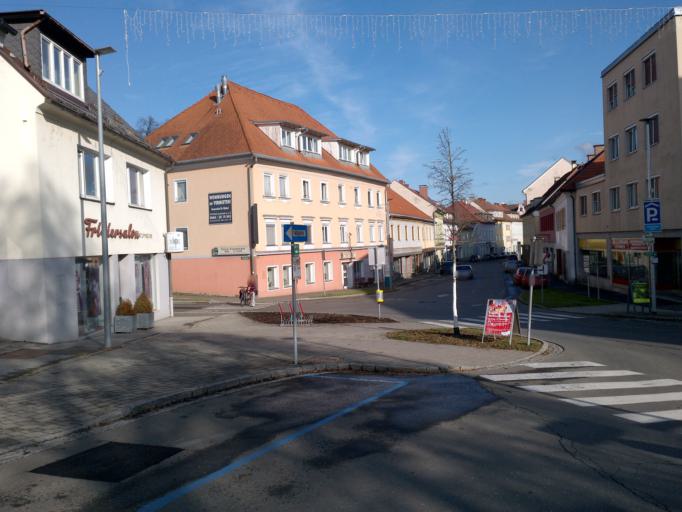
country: AT
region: Styria
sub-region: Politischer Bezirk Murtal
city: Knittelfeld
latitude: 47.2153
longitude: 14.8318
